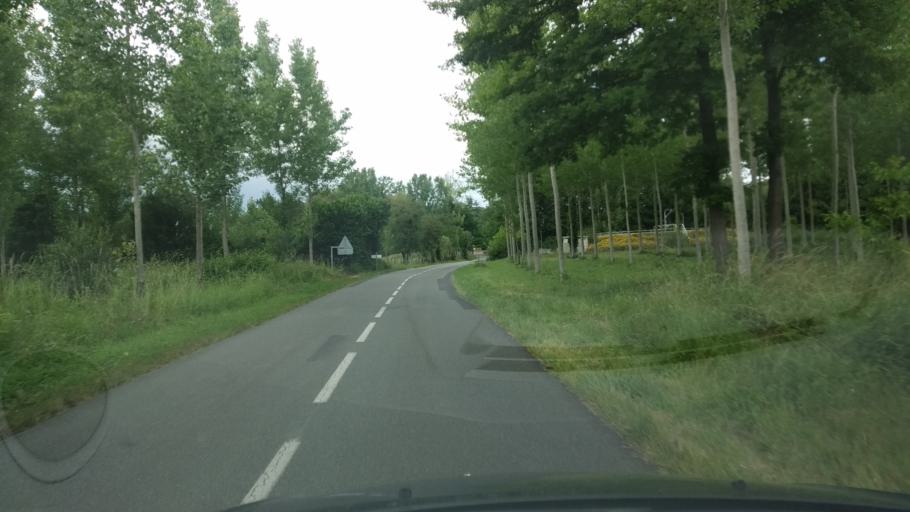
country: FR
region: Poitou-Charentes
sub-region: Departement de la Vienne
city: Vouille
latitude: 46.6345
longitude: 0.1677
